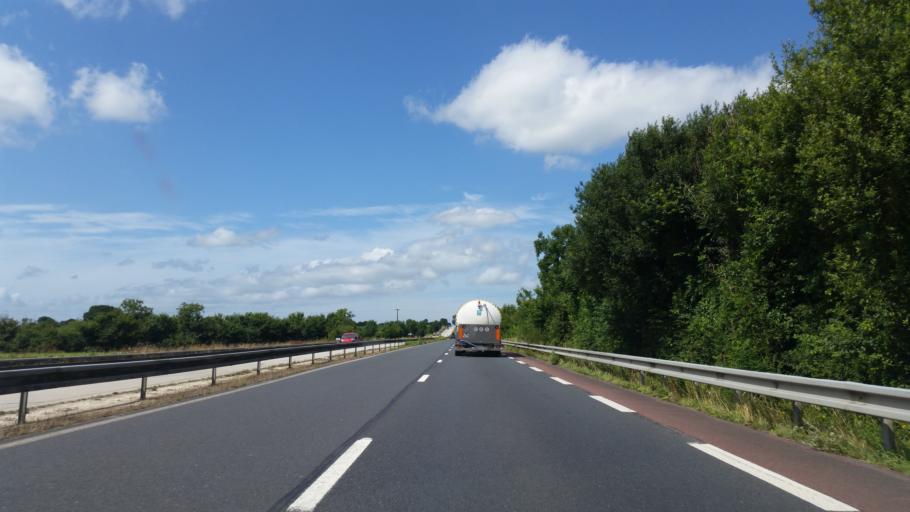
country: FR
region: Lower Normandy
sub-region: Departement de la Manche
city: Sainte-Mere-Eglise
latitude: 49.4466
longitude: -1.3469
